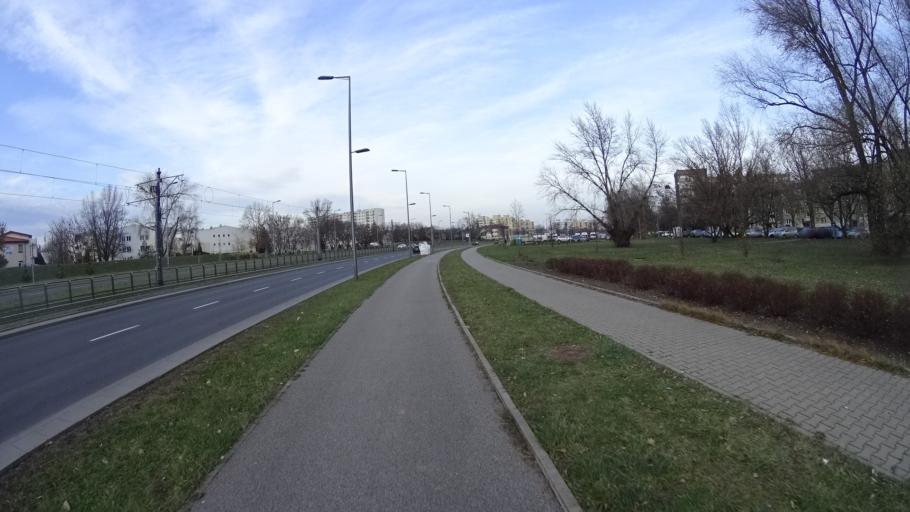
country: PL
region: Masovian Voivodeship
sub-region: Warszawa
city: Bemowo
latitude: 52.2490
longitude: 20.9112
